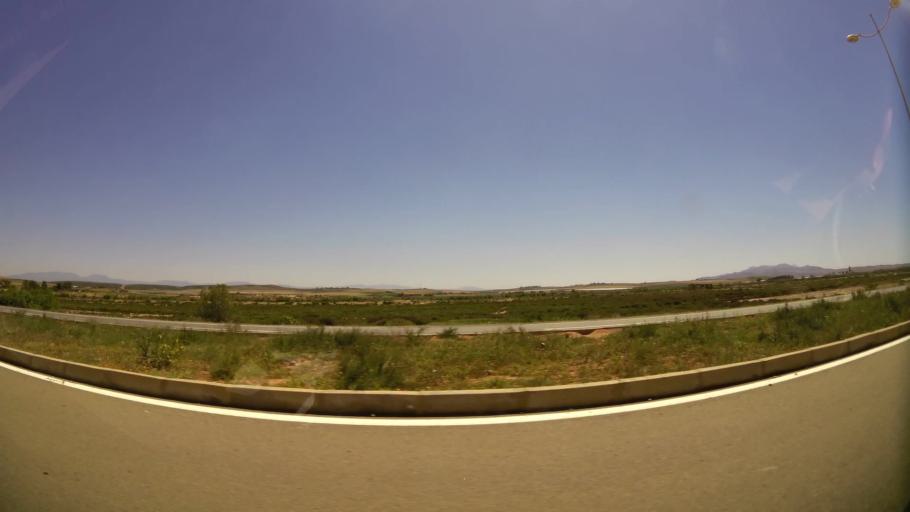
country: MA
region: Oriental
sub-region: Berkane-Taourirt
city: Madagh
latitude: 35.1022
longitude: -2.3378
